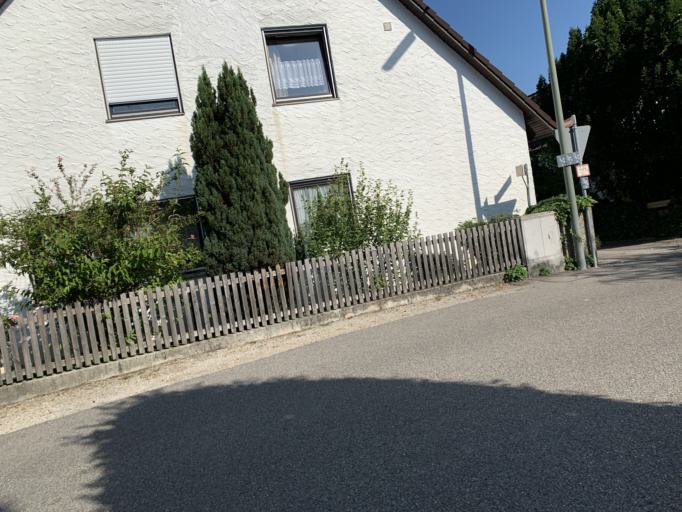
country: DE
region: Bavaria
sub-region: Upper Bavaria
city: Freising
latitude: 48.4086
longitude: 11.7558
